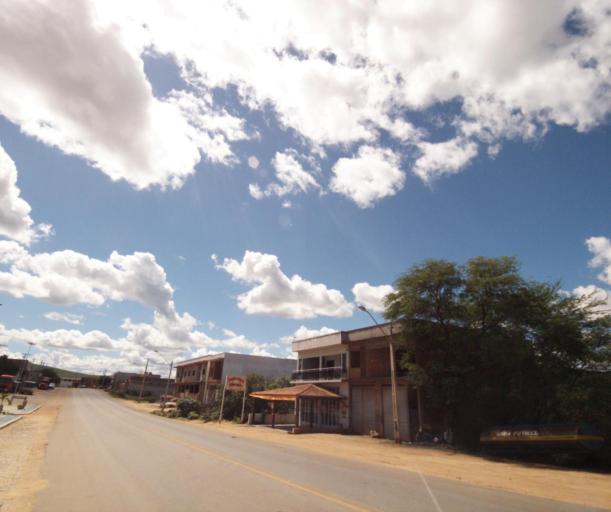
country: BR
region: Bahia
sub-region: Cacule
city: Cacule
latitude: -14.2053
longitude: -42.1163
